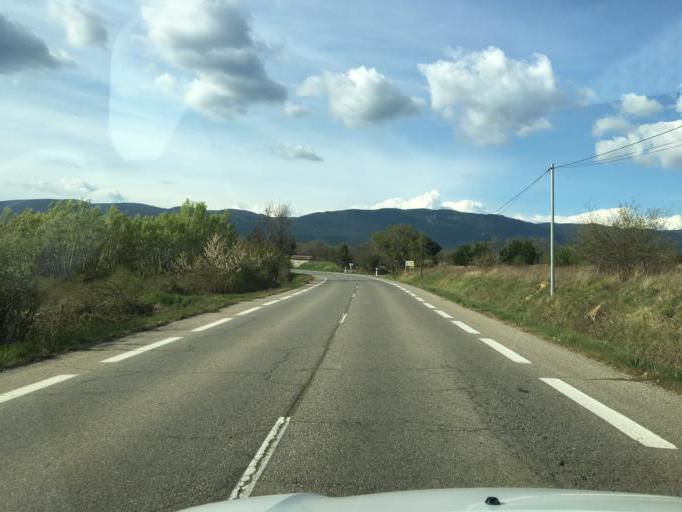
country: FR
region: Provence-Alpes-Cote d'Azur
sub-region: Departement du Vaucluse
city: Ansouis
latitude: 43.7548
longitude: 5.4609
